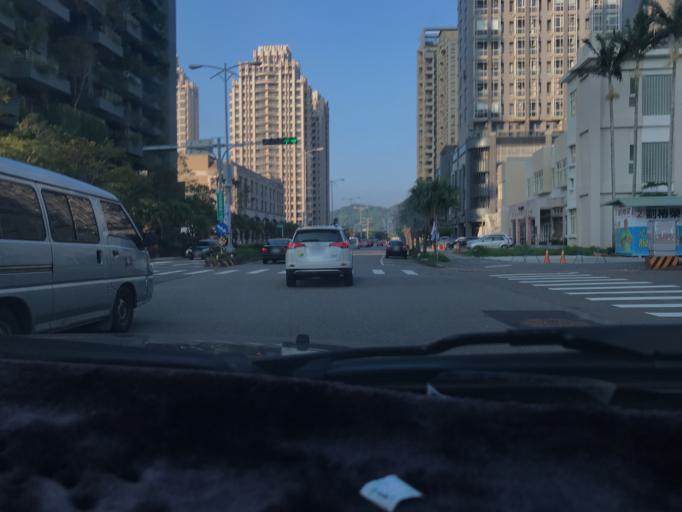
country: TW
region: Taiwan
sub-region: Hsinchu
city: Zhubei
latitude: 24.8109
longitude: 121.0344
